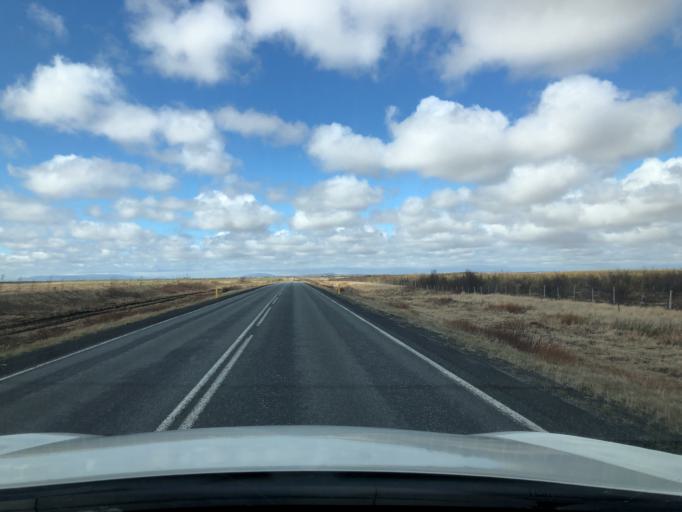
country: IS
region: South
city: Vestmannaeyjar
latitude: 63.8054
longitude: -20.3303
